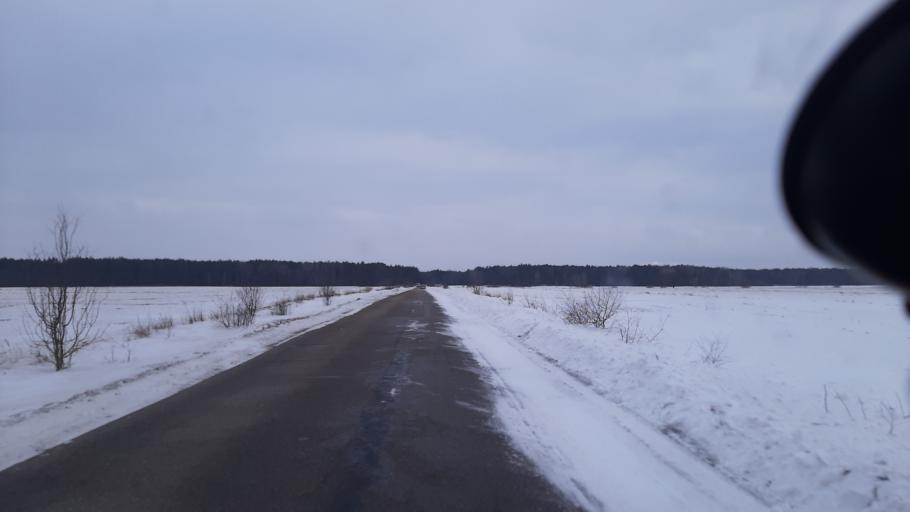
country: PL
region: Lublin Voivodeship
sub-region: Powiat lubartowski
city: Abramow
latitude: 51.4432
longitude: 22.2656
